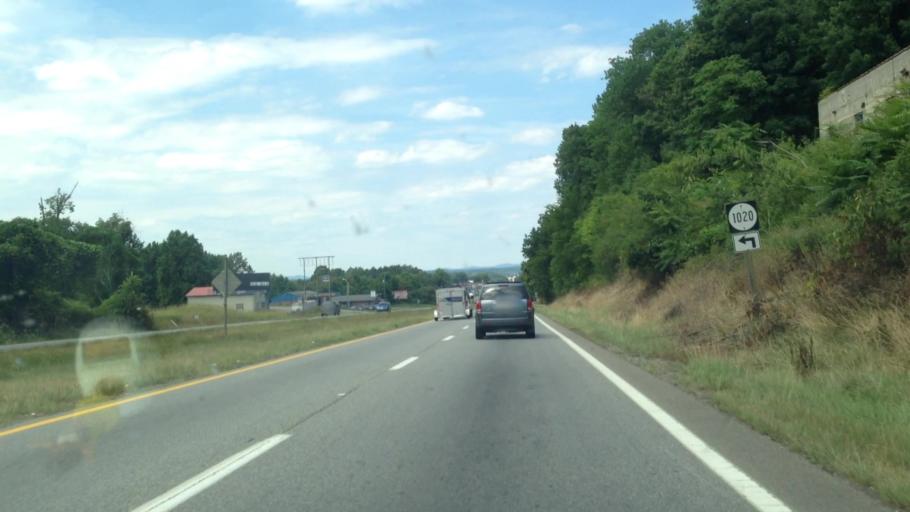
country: US
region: Virginia
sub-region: Henry County
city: Chatmoss
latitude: 36.5888
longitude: -79.8630
